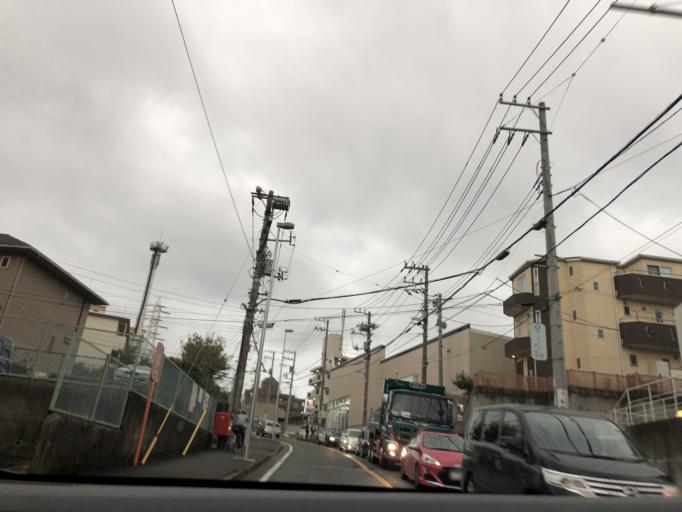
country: JP
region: Kanagawa
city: Yokohama
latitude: 35.5167
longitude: 139.6476
